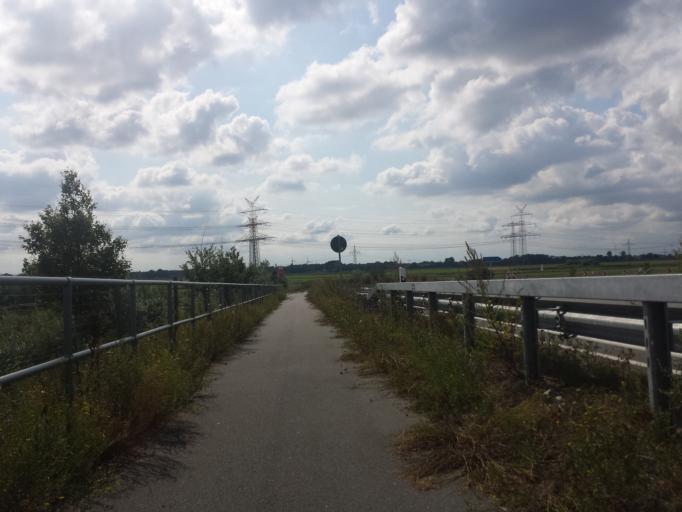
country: DE
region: Lower Saxony
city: Delmenhorst
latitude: 53.0965
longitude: 8.6887
